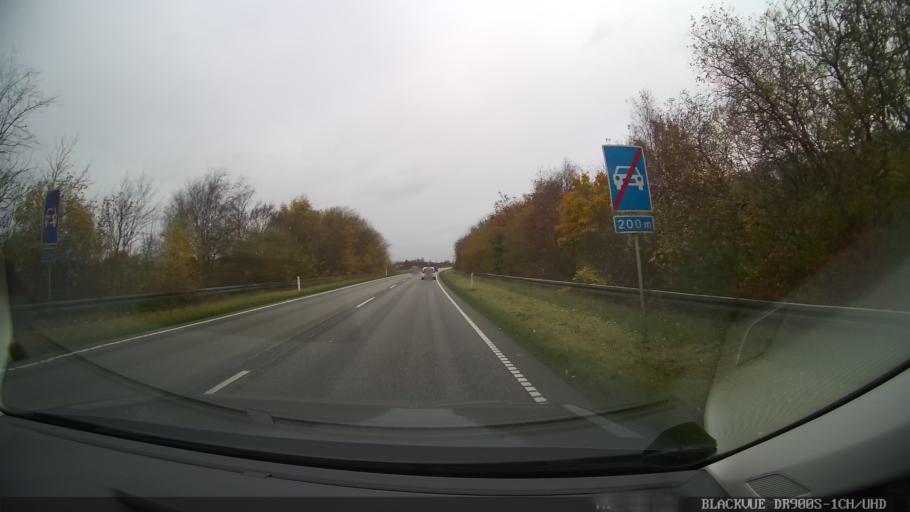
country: DK
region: North Denmark
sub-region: Thisted Kommune
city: Thisted
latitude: 56.8369
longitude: 8.7049
